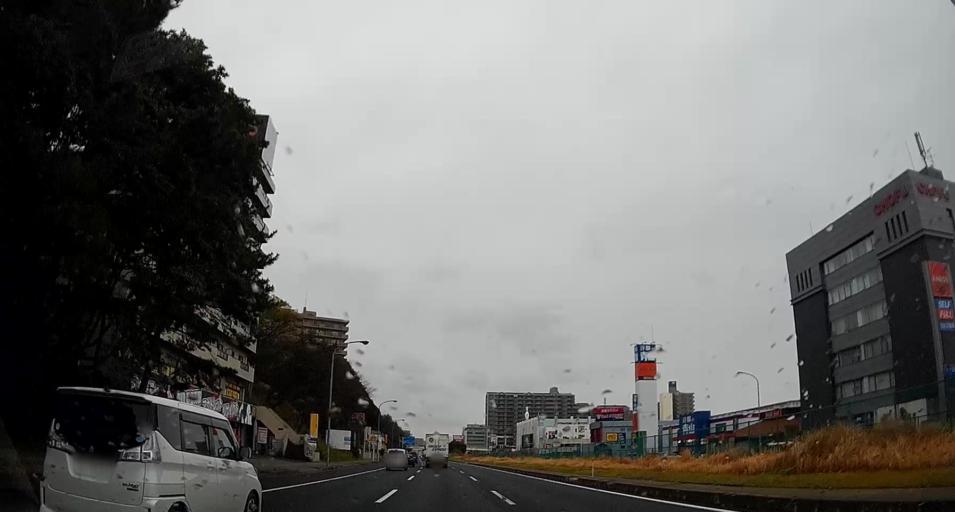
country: JP
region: Chiba
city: Chiba
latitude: 35.6214
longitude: 140.0954
